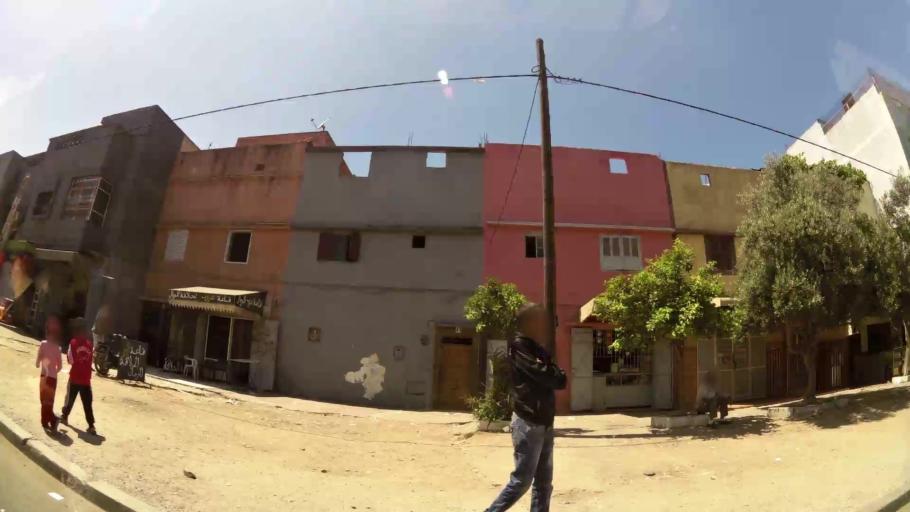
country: MA
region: Gharb-Chrarda-Beni Hssen
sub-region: Kenitra Province
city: Kenitra
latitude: 34.2491
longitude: -6.5420
